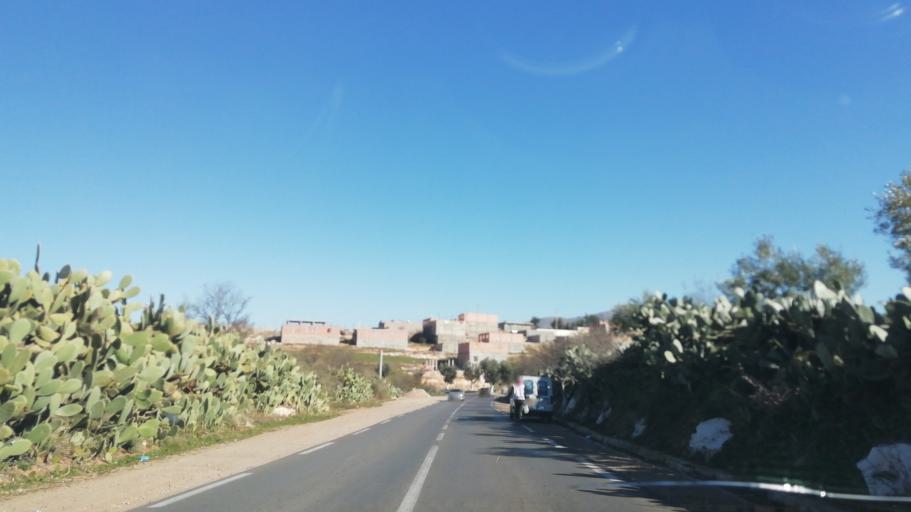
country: DZ
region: Tlemcen
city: Beni Mester
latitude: 34.8402
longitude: -1.4775
